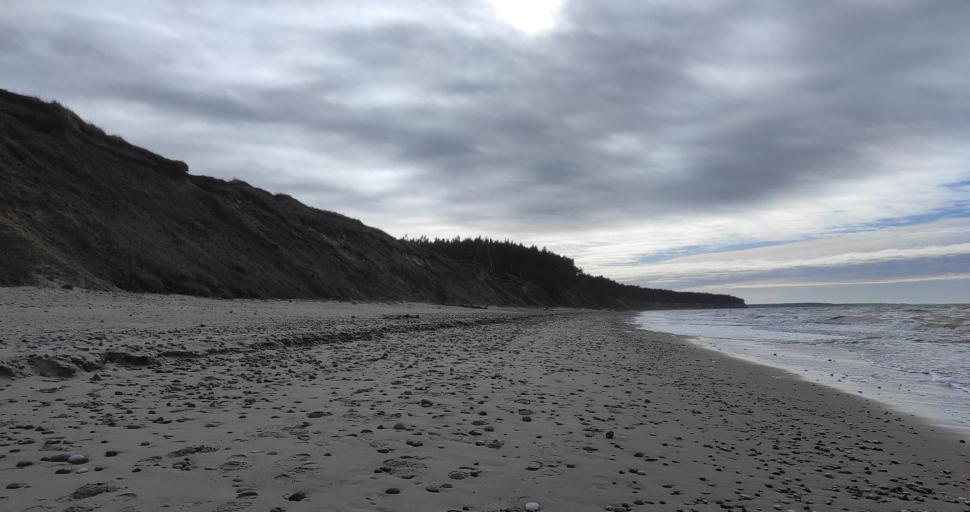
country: LV
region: Alsunga
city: Alsunga
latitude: 57.0351
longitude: 21.4007
